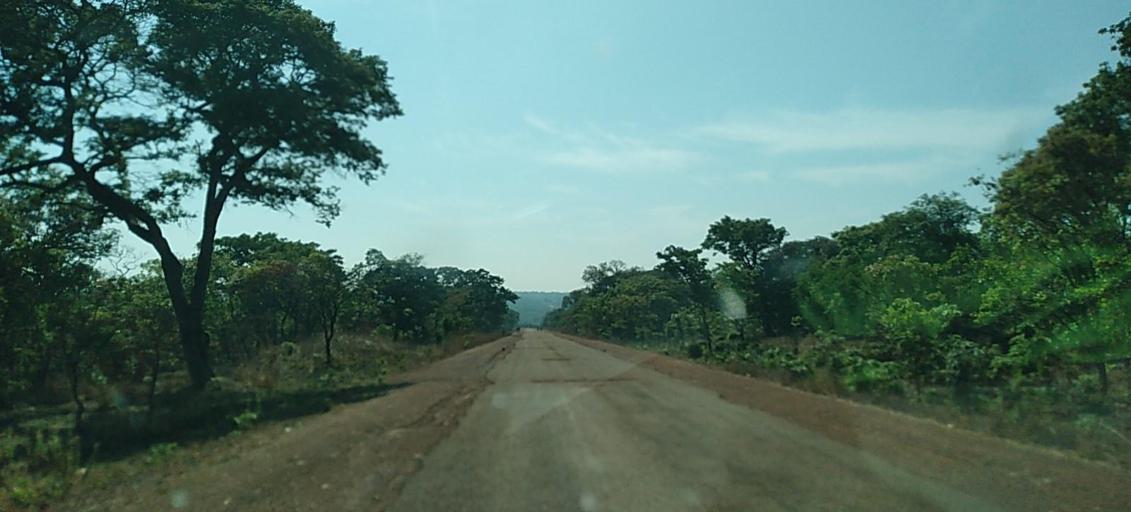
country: ZM
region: North-Western
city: Mwinilunga
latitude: -11.8228
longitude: 25.1129
